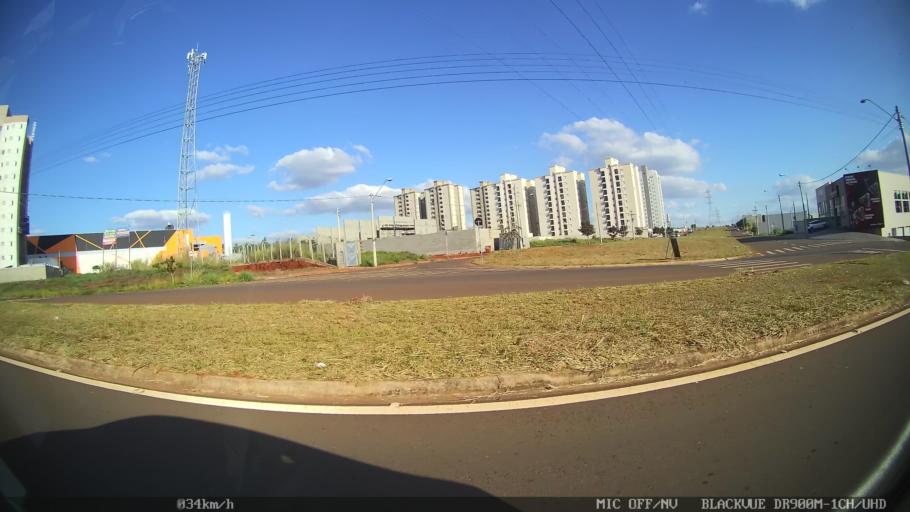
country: BR
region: Sao Paulo
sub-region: Santa Barbara D'Oeste
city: Santa Barbara d'Oeste
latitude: -22.7574
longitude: -47.4341
